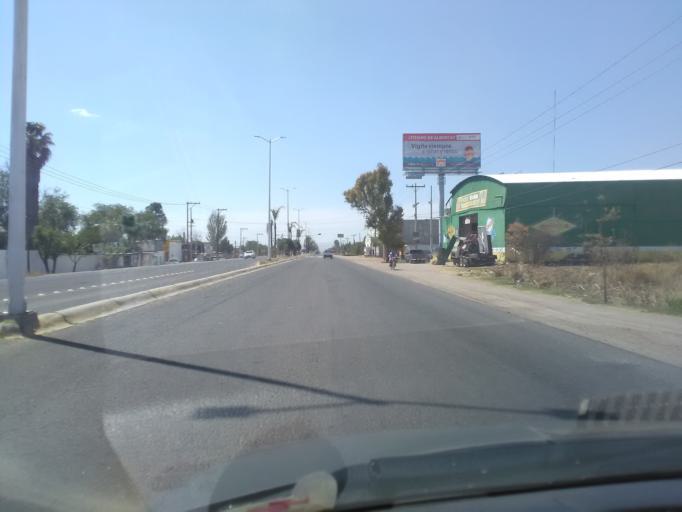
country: MX
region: Durango
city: Victoria de Durango
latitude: 24.0265
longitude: -104.5759
